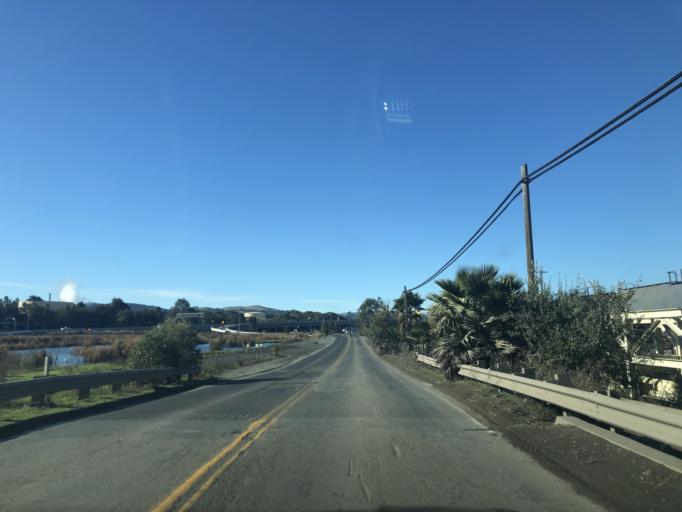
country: US
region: California
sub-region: Contra Costa County
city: Vine Hill
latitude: 38.0259
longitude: -122.1054
